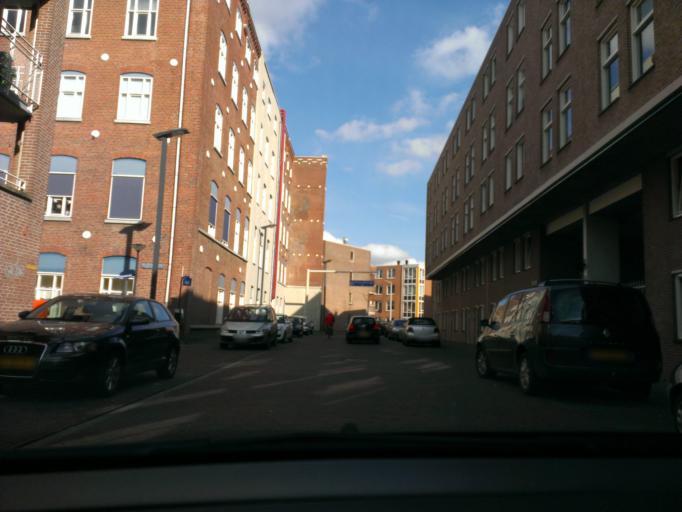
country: NL
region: Overijssel
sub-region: Gemeente Enschede
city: Enschede
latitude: 52.2225
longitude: 6.8970
